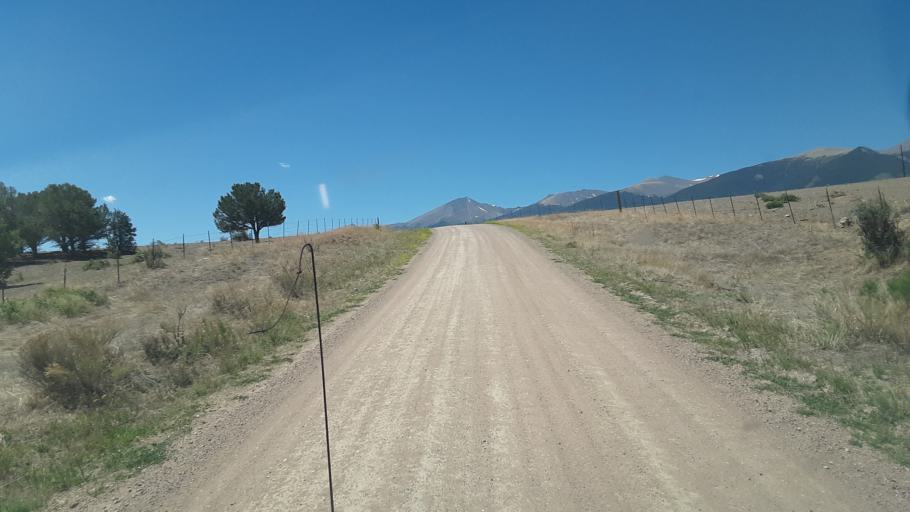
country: US
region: Colorado
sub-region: Custer County
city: Westcliffe
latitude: 38.3021
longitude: -105.6153
